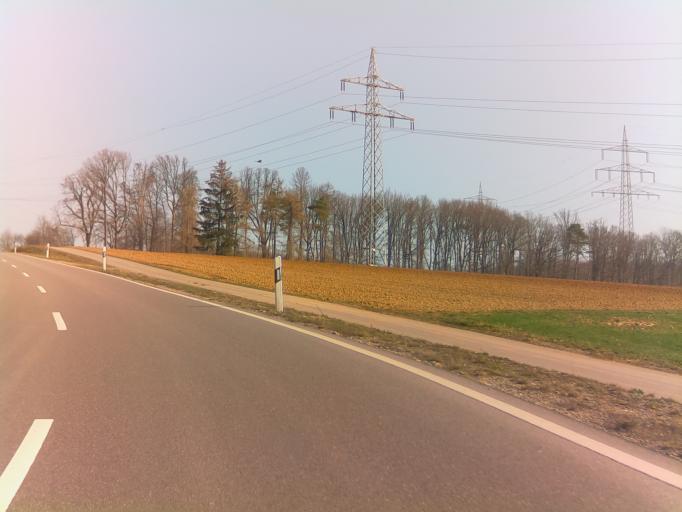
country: DE
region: Baden-Wuerttemberg
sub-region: Regierungsbezirk Stuttgart
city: Eberdingen
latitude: 48.8725
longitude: 8.9987
